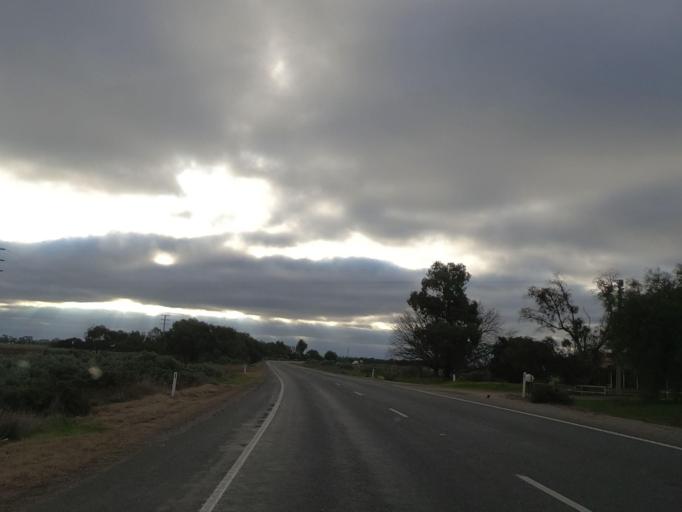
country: AU
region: Victoria
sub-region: Swan Hill
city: Swan Hill
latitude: -35.7235
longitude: 143.8892
